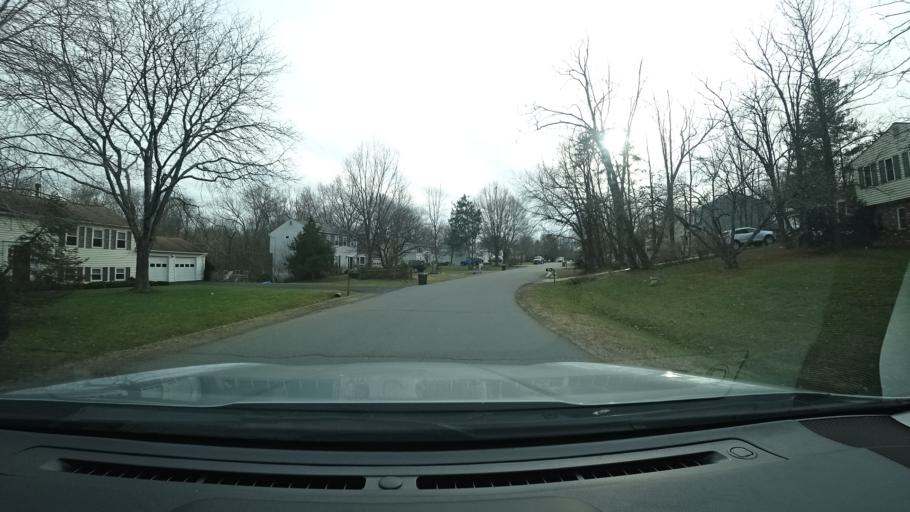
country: US
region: Virginia
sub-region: Fairfax County
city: Oak Hill
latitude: 38.9419
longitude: -77.3795
